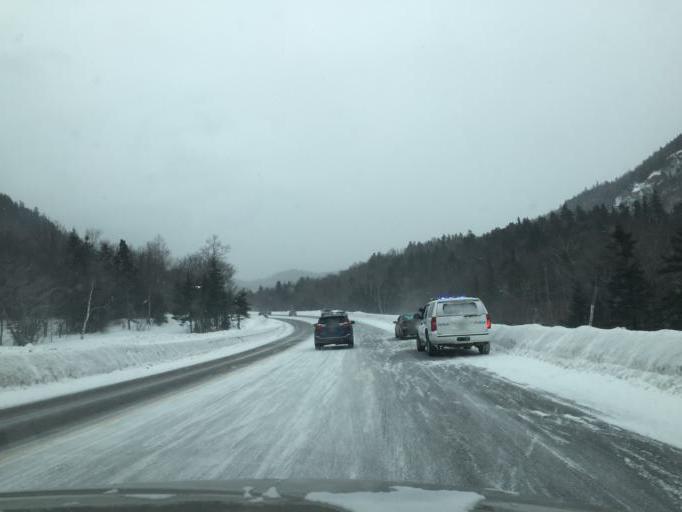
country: US
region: New Hampshire
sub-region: Coos County
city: Gorham
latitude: 44.2452
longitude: -71.2534
